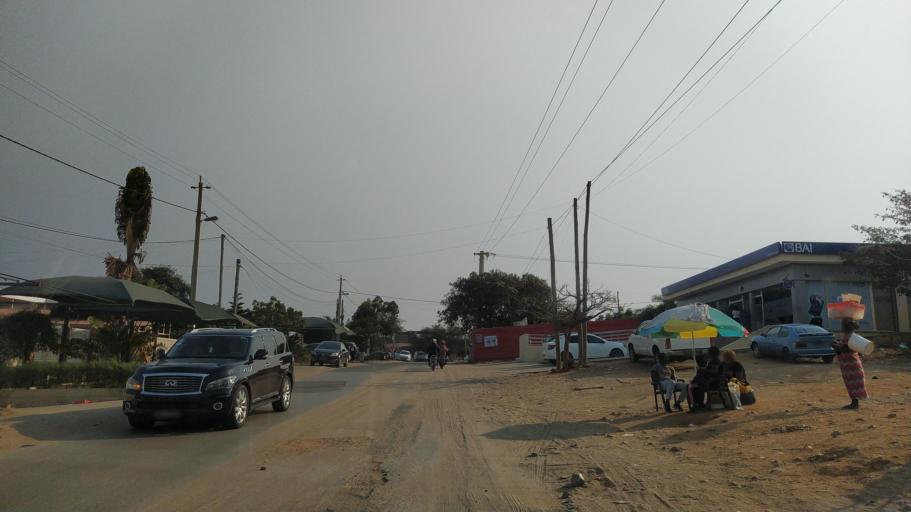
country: AO
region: Luanda
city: Luanda
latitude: -8.9116
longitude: 13.2256
